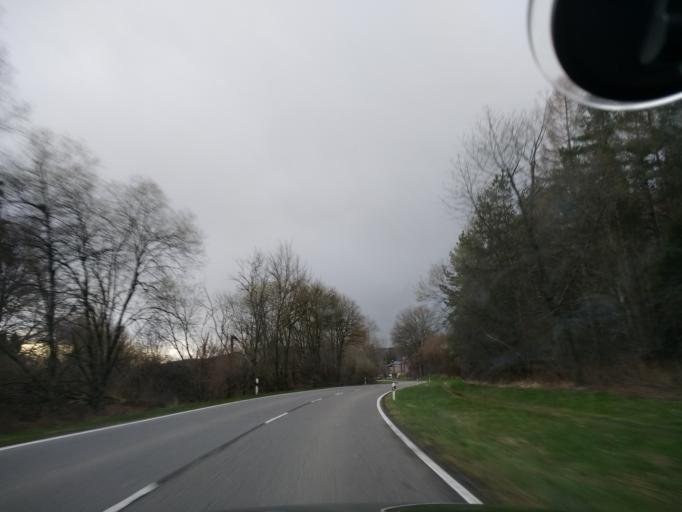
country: DE
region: Baden-Wuerttemberg
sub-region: Freiburg Region
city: Allensbach
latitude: 47.7269
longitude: 9.1218
